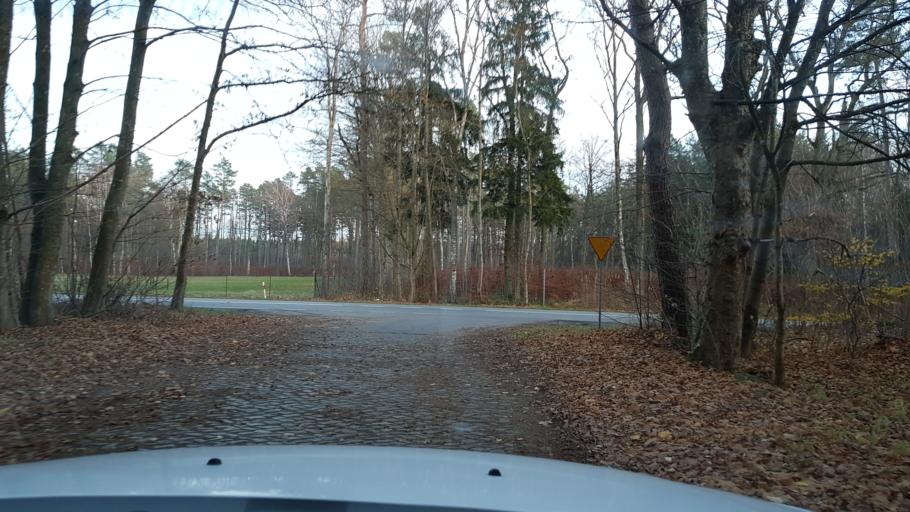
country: PL
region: West Pomeranian Voivodeship
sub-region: Koszalin
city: Koszalin
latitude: 54.0971
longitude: 16.1626
